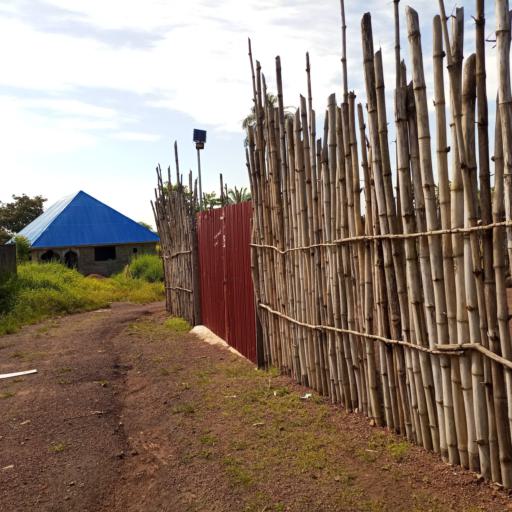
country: SL
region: Northern Province
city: Kambia
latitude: 9.1234
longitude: -12.9134
